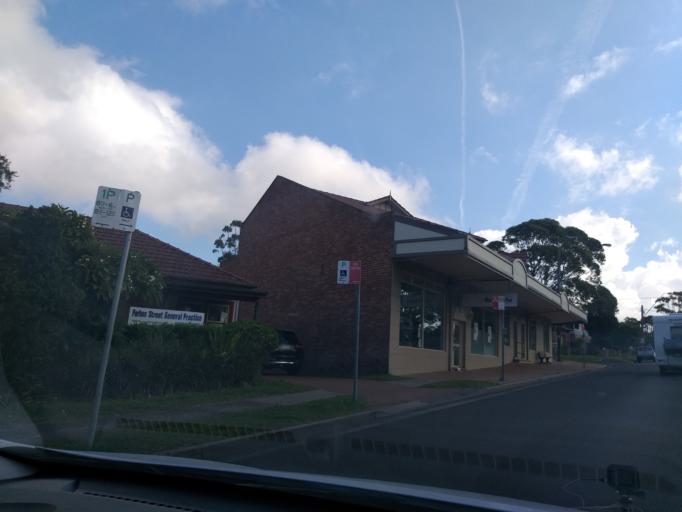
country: AU
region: New South Wales
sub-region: Wollongong
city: Helensburgh
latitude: -34.1909
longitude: 150.9811
